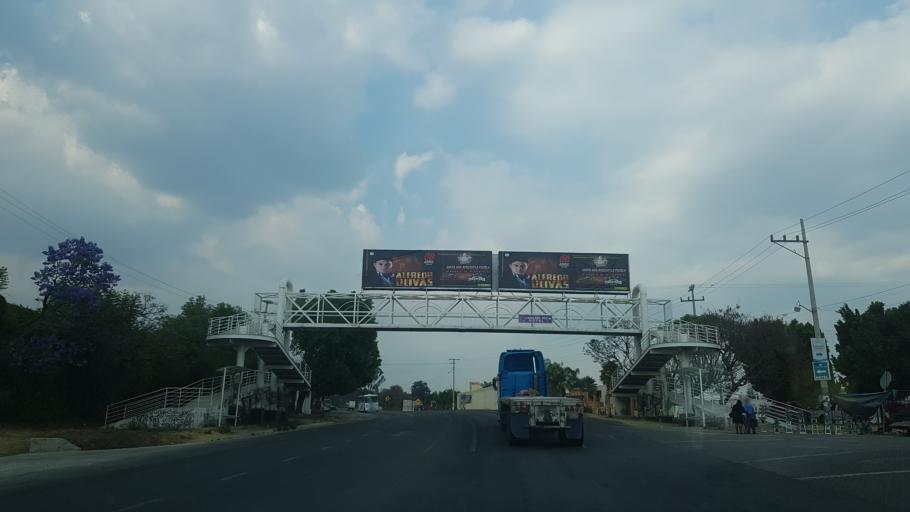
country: MX
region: Puebla
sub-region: Santa Isabel Cholula
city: Santa Ana Acozautla
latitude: 18.9566
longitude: -98.3873
